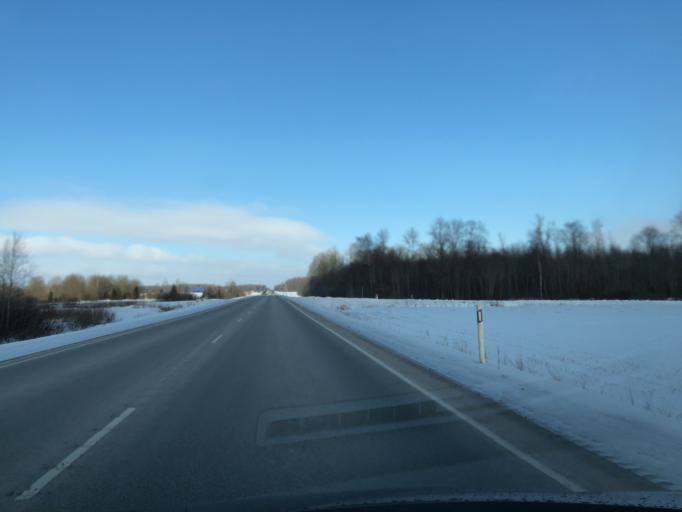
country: EE
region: Jaervamaa
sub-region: Paide linn
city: Paide
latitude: 58.7919
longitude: 25.7582
